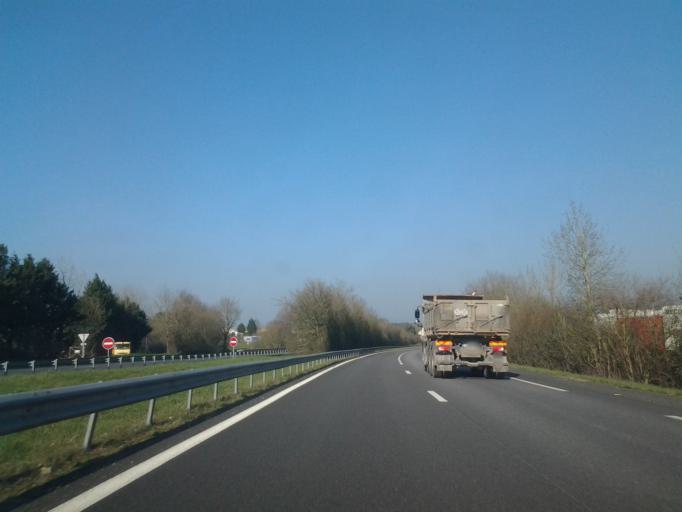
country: FR
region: Pays de la Loire
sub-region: Departement de la Vendee
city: La Genetouze
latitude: 46.7197
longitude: -1.5503
